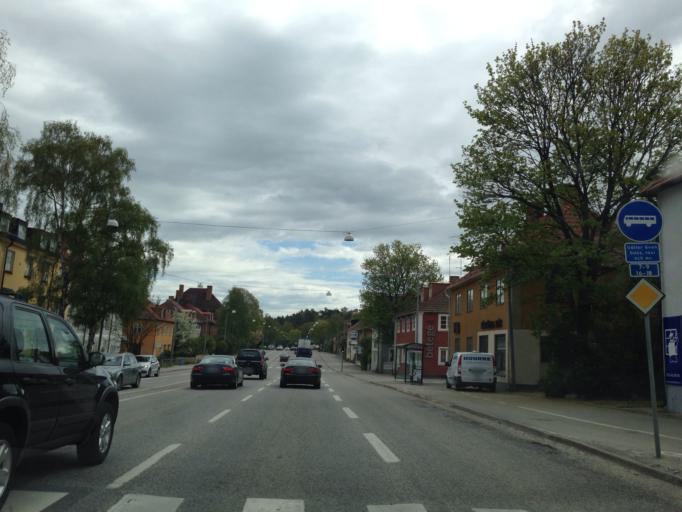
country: SE
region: Stockholm
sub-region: Sundbybergs Kommun
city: Sundbyberg
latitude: 59.3379
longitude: 17.9651
